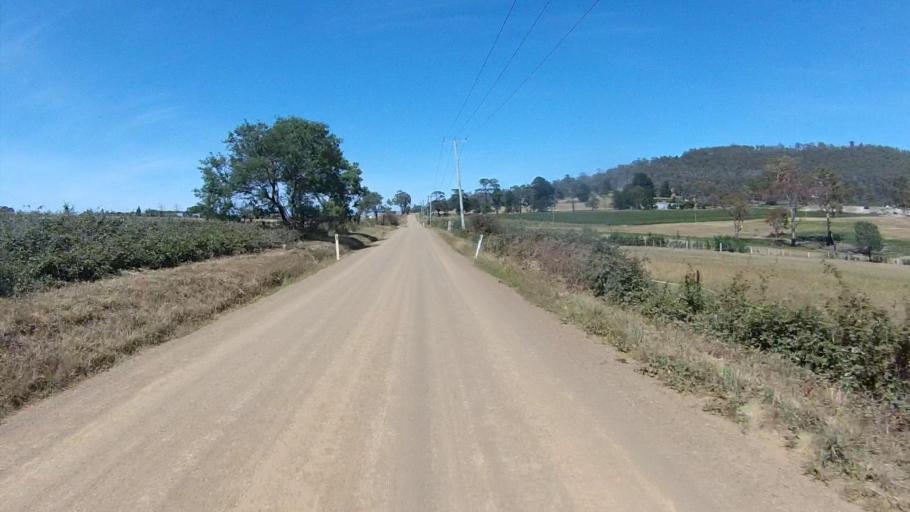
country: AU
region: Tasmania
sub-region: Sorell
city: Sorell
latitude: -42.7842
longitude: 147.6389
